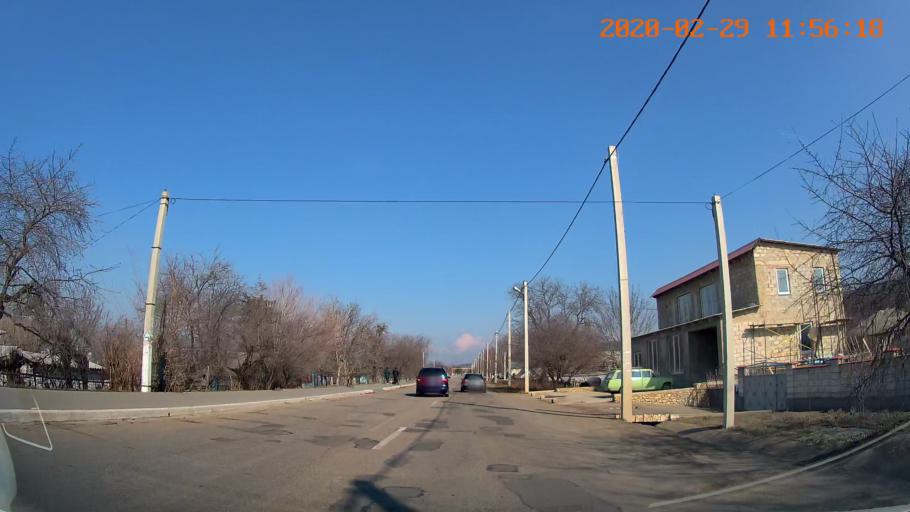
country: MD
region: Telenesti
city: Ribnita
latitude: 47.7954
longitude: 29.0013
